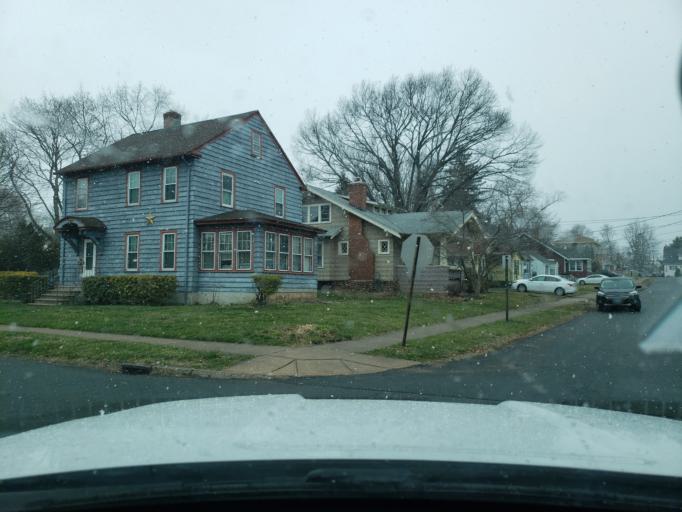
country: US
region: Connecticut
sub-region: Hartford County
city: New Britain
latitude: 41.6893
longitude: -72.7730
